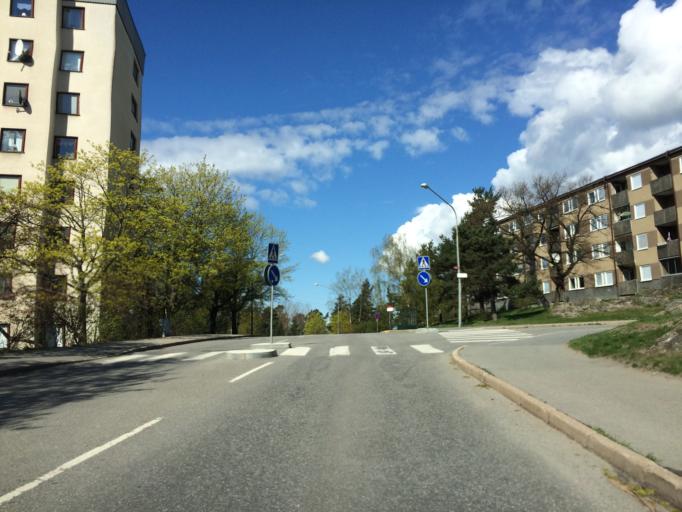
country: SE
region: Stockholm
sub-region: Huddinge Kommun
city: Segeltorp
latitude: 59.2980
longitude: 17.9314
